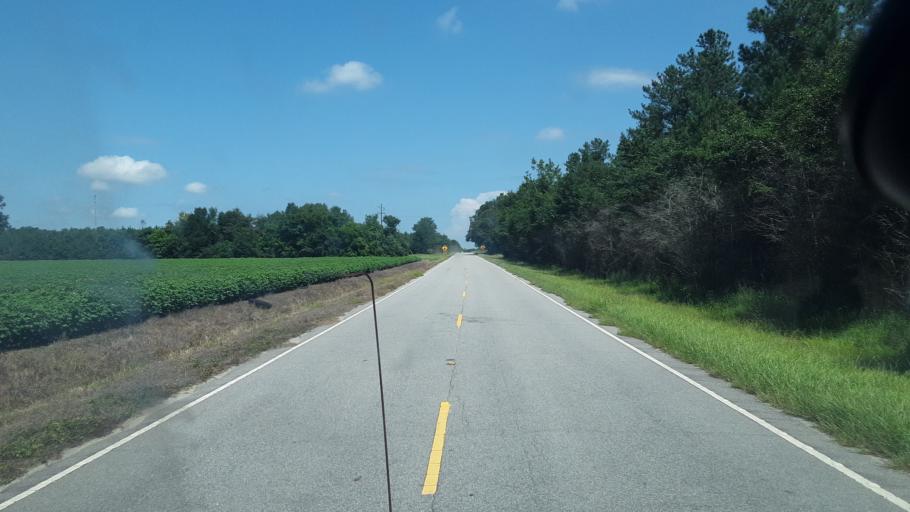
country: US
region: South Carolina
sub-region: Bamberg County
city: Bamberg
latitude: 33.4029
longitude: -81.0157
